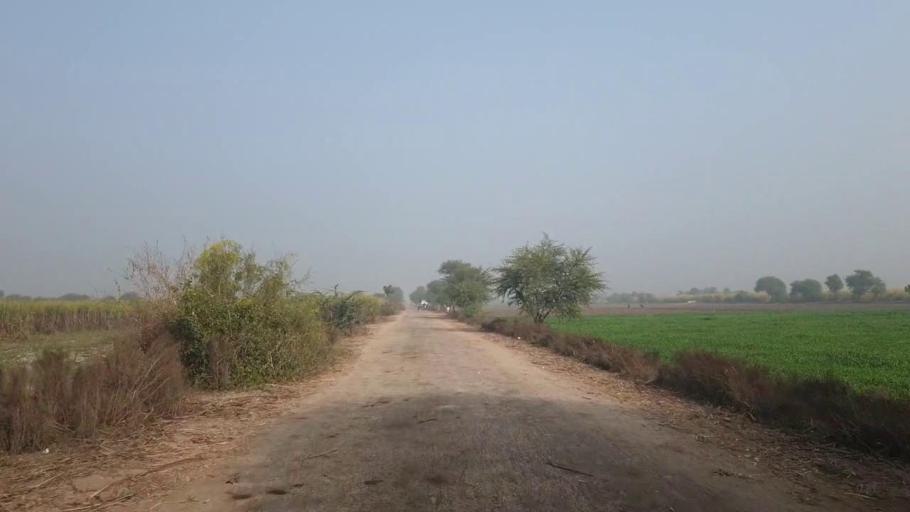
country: PK
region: Sindh
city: Tando Adam
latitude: 25.8135
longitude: 68.6153
